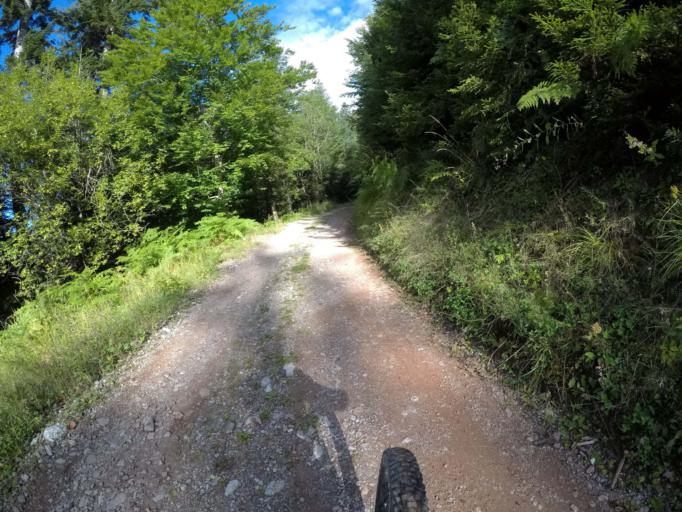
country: IT
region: Friuli Venezia Giulia
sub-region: Provincia di Udine
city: Paularo
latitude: 46.5390
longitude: 13.0979
